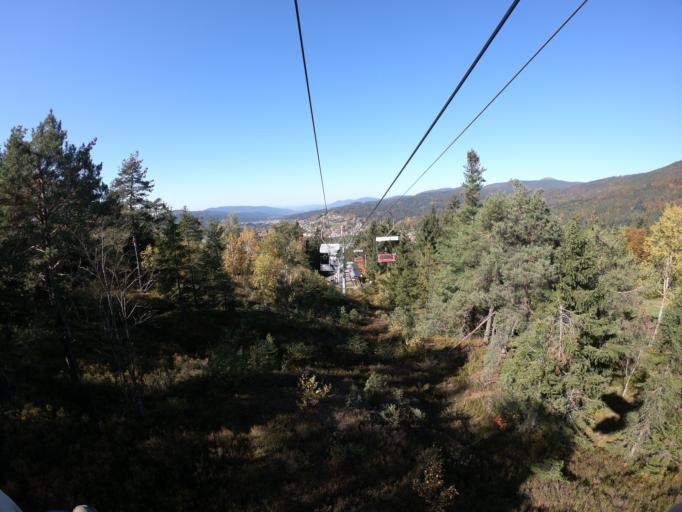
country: DE
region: Bavaria
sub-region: Lower Bavaria
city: Bodenmais
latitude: 49.0587
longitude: 13.1237
